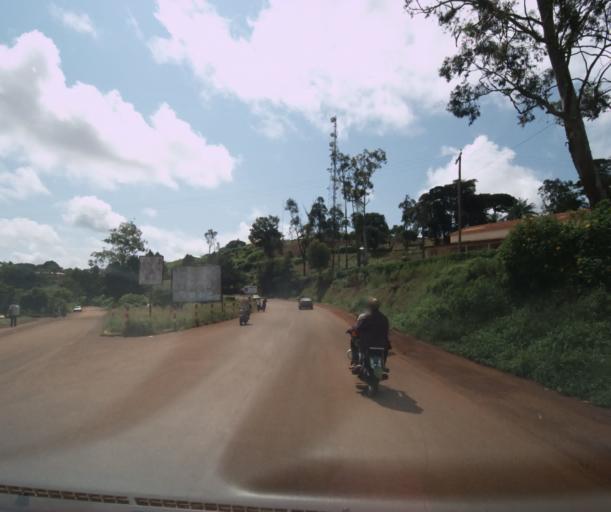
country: CM
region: West
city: Foumban
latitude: 5.7311
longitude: 10.8790
